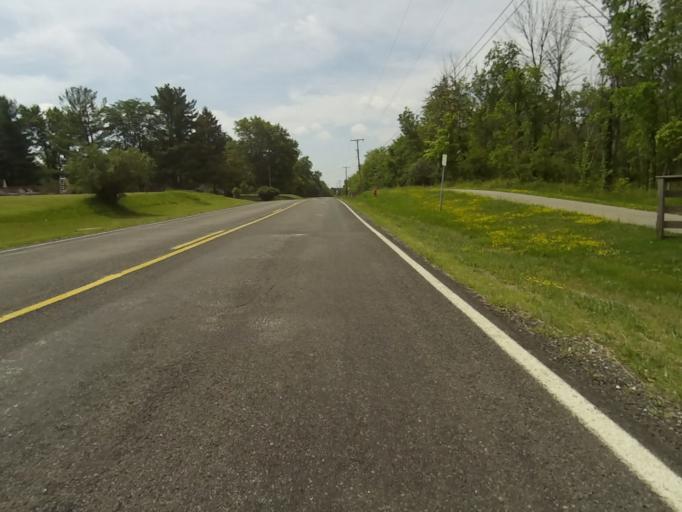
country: US
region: Ohio
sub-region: Summit County
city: Boston Heights
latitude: 41.2831
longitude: -81.5386
